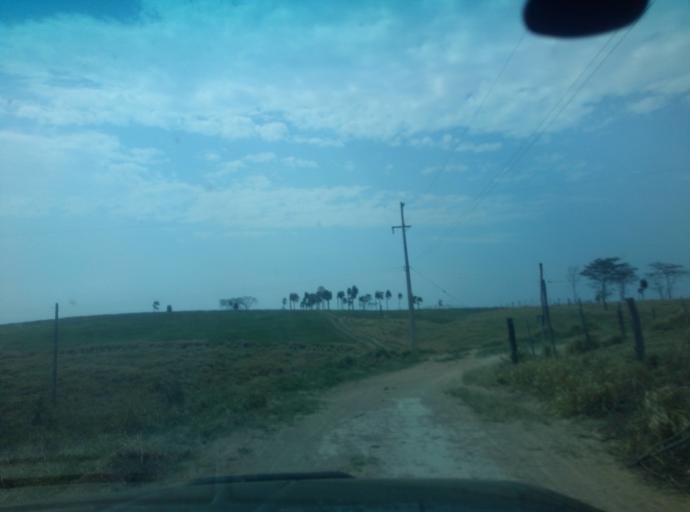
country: PY
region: Caaguazu
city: Doctor Cecilio Baez
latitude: -25.1378
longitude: -56.1585
